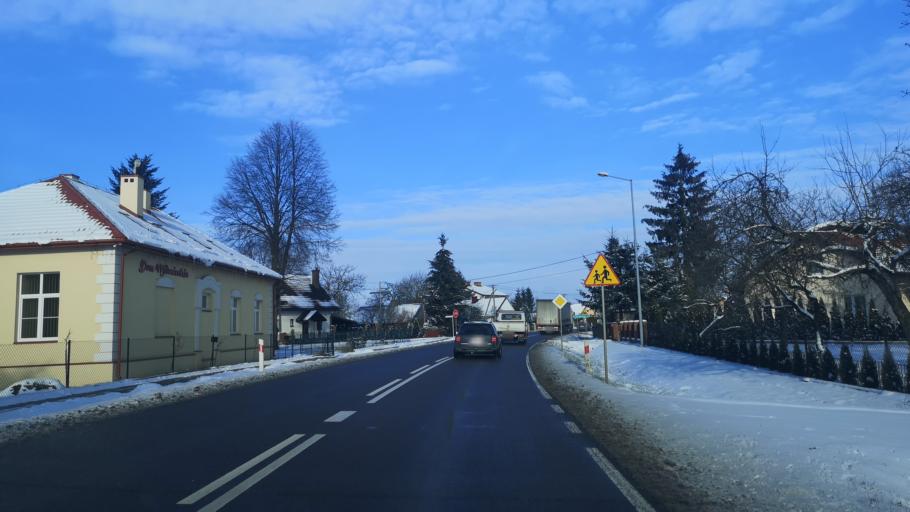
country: PL
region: Subcarpathian Voivodeship
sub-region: Powiat przeworski
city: Tryncza
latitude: 50.1358
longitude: 22.5371
